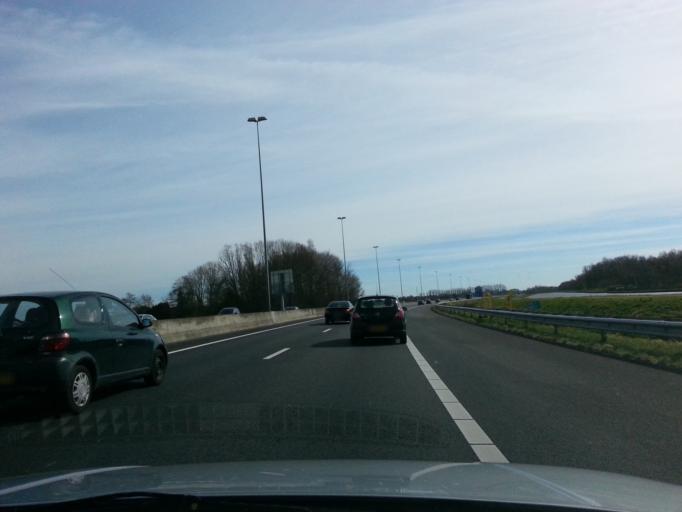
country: NL
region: Groningen
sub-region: Gemeente Groningen
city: Groningen
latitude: 53.1837
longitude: 6.5741
